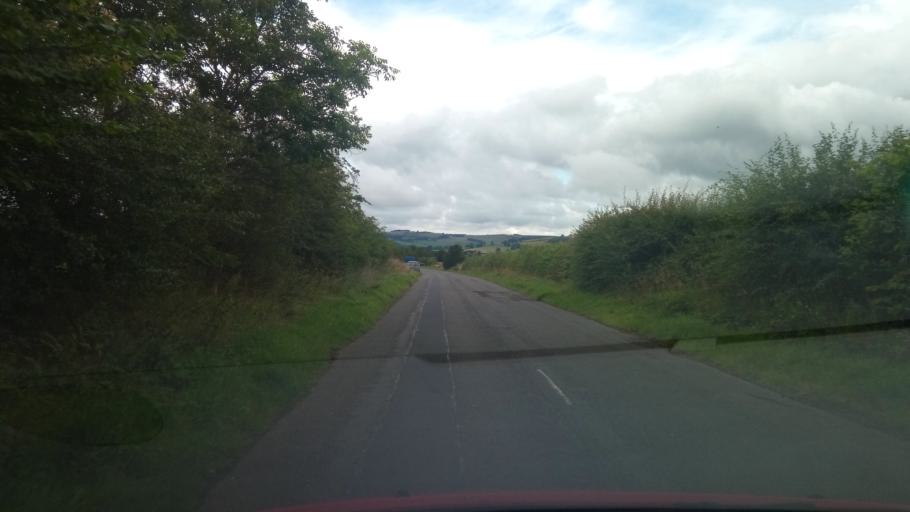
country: GB
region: Scotland
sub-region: The Scottish Borders
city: Newtown St Boswells
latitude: 55.5958
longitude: -2.7007
